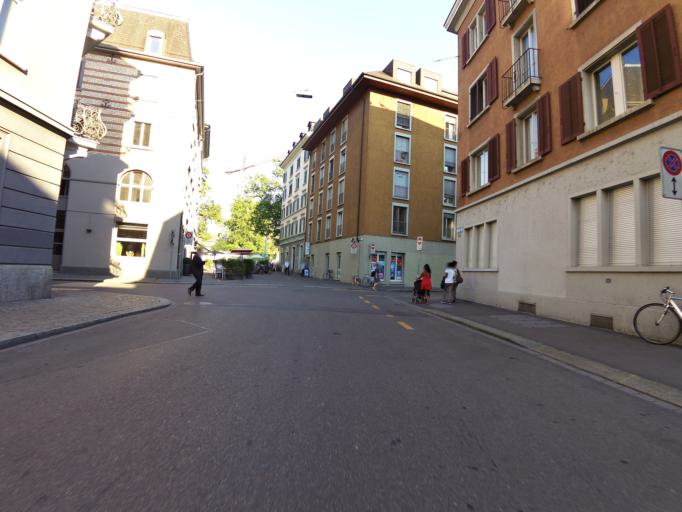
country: CH
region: Zurich
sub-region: Bezirk Zuerich
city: Zuerich (Kreis 1) / City
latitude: 47.3802
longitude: 8.5367
